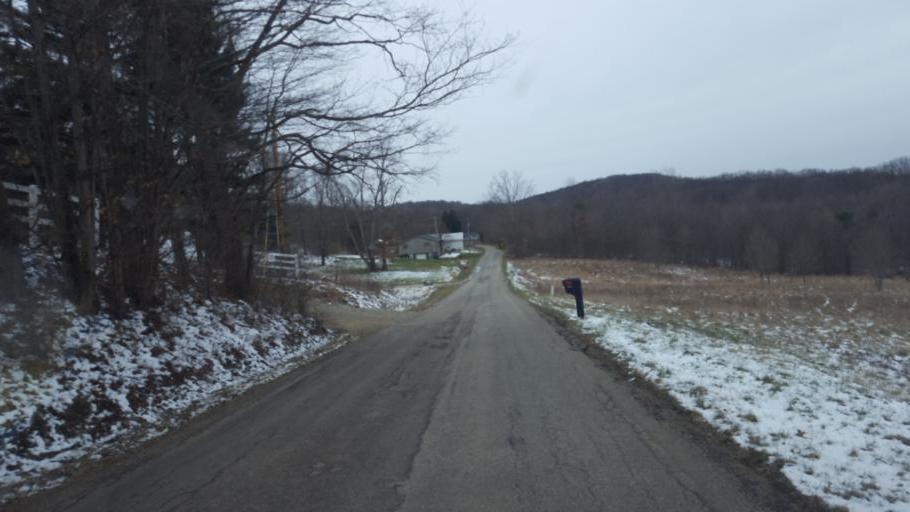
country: US
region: Ohio
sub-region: Sandusky County
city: Bellville
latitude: 40.5869
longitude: -82.4459
